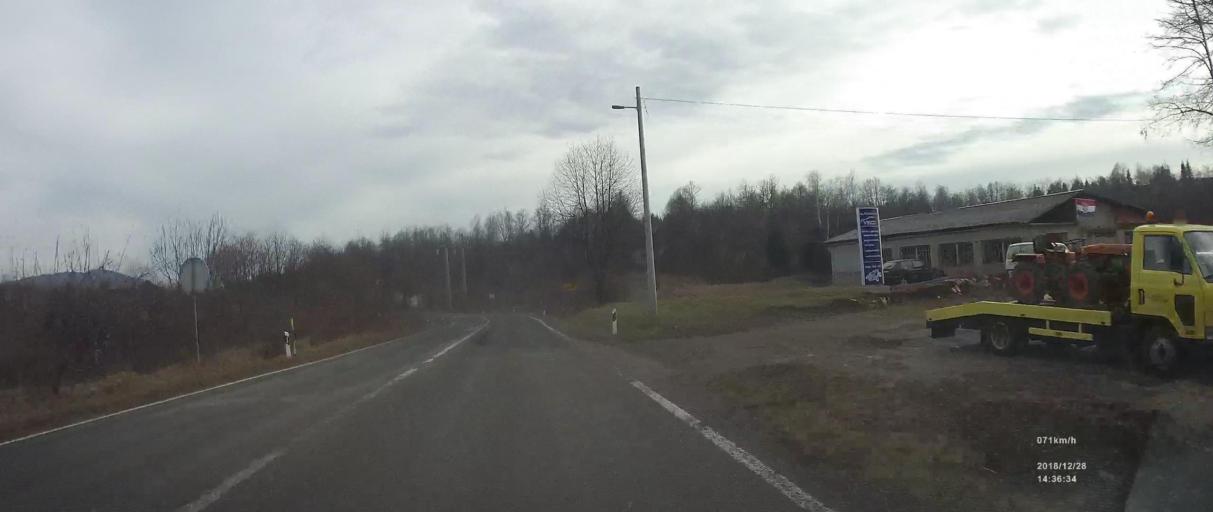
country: HR
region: Primorsko-Goranska
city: Vrbovsko
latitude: 45.4222
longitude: 15.1984
